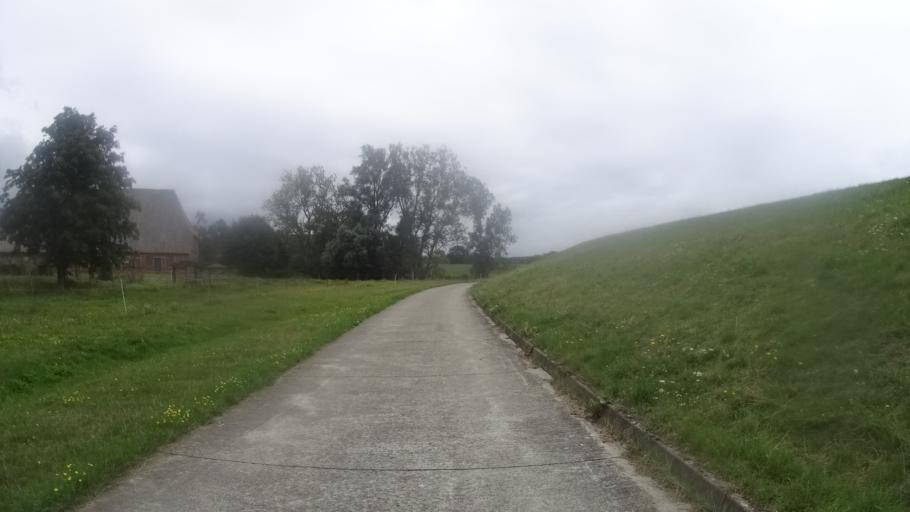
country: DE
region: Lower Saxony
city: Tosterglope
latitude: 53.2725
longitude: 10.8272
